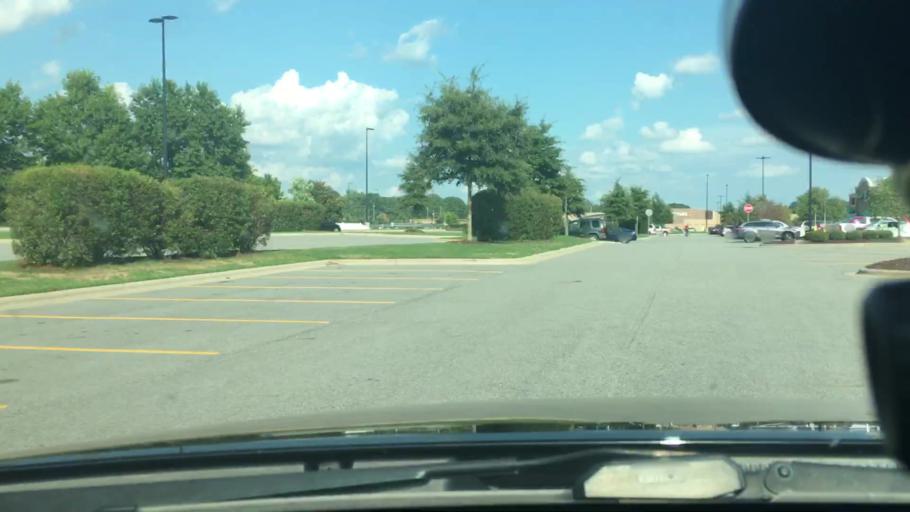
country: US
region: North Carolina
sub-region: Pitt County
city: Windsor
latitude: 35.5811
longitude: -77.3109
